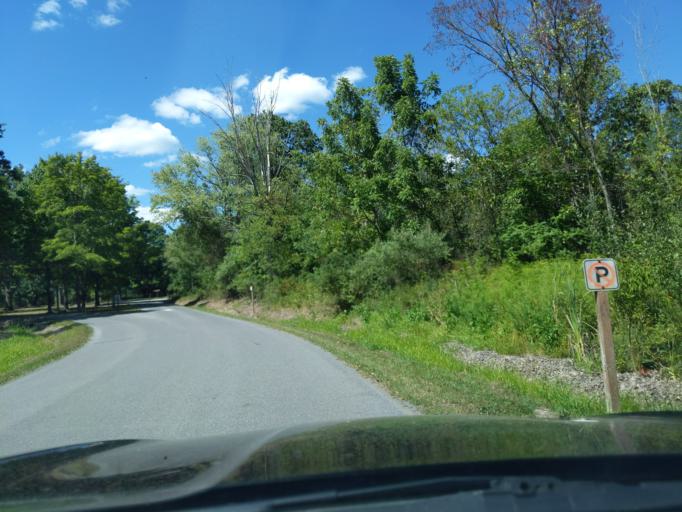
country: US
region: Pennsylvania
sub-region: Blair County
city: Greenwood
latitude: 40.4791
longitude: -78.2895
